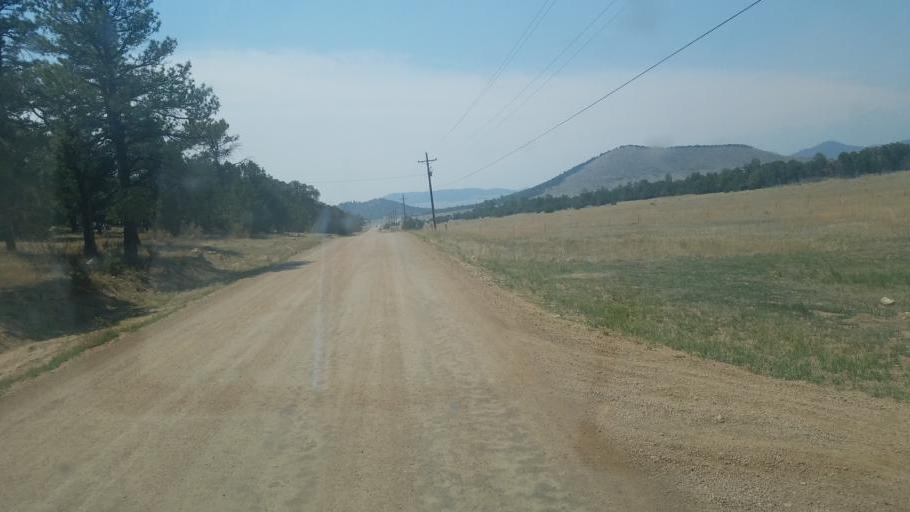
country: US
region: Colorado
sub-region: Custer County
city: Westcliffe
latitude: 38.3167
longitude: -105.4870
